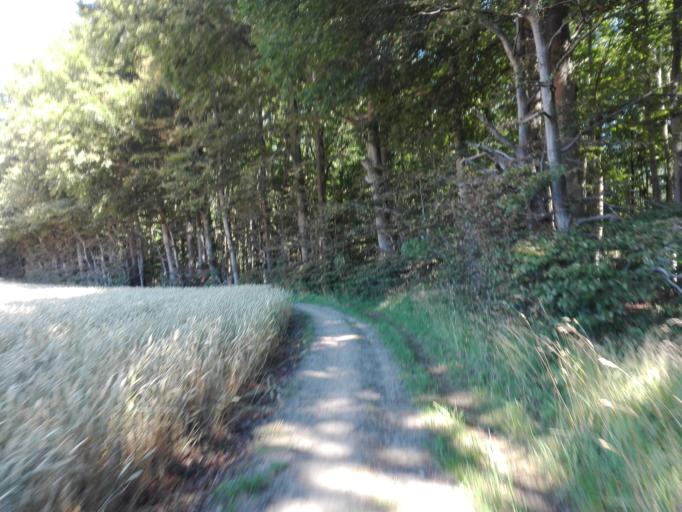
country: DK
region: Central Jutland
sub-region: Odder Kommune
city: Odder
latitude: 55.9645
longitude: 10.1391
